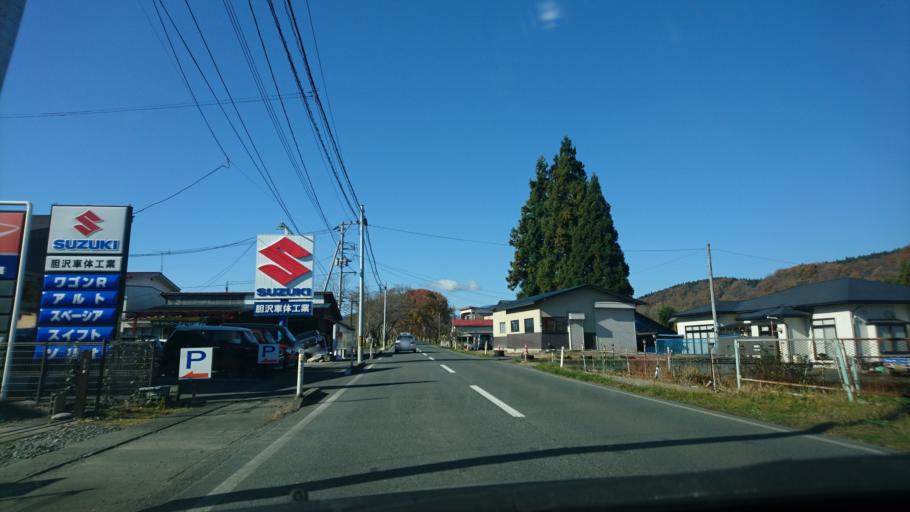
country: JP
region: Iwate
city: Mizusawa
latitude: 39.1292
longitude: 141.0294
